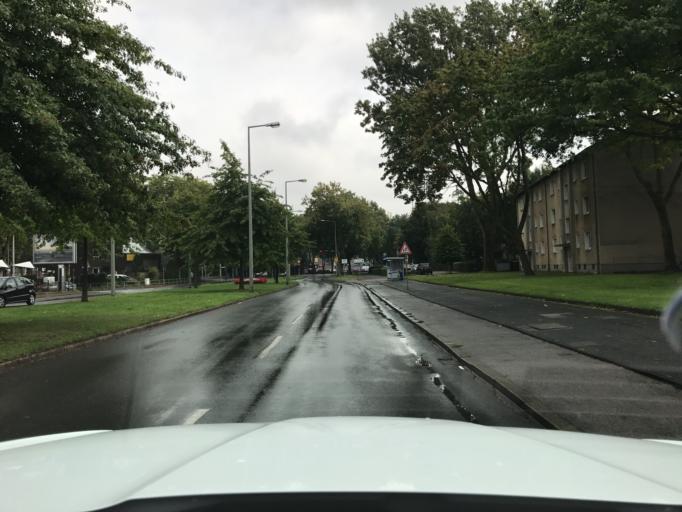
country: DE
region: North Rhine-Westphalia
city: Meiderich
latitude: 51.4657
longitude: 6.7906
